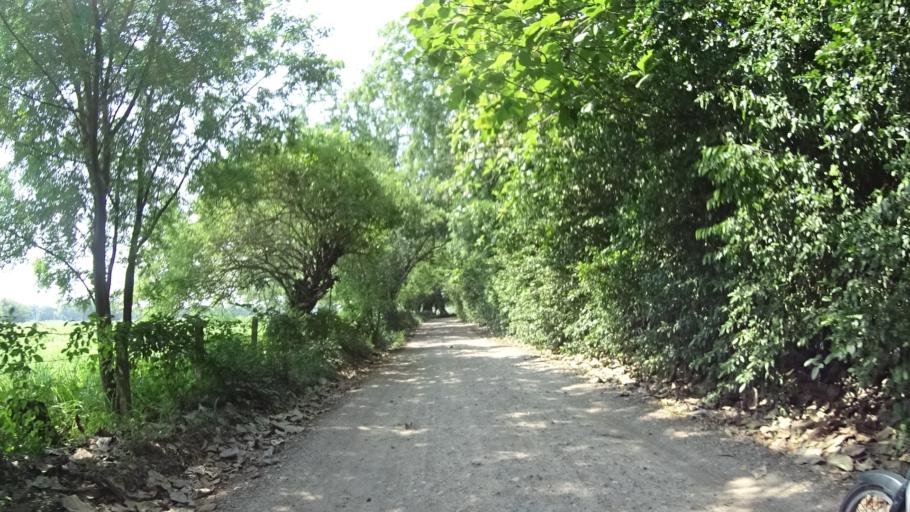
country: CO
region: Cundinamarca
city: Puerto Salgar
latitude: 5.5125
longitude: -74.6883
